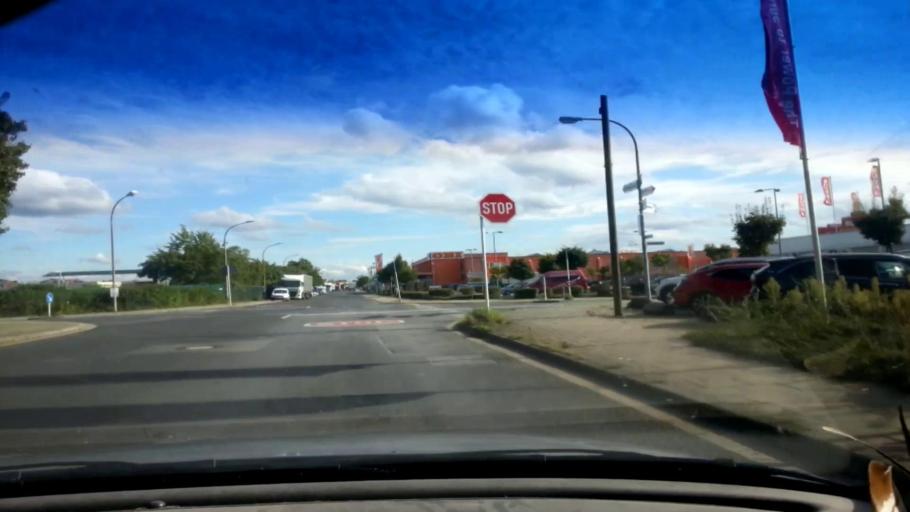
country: DE
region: Bavaria
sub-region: Upper Franconia
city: Hallstadt
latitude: 49.9129
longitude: 10.8758
